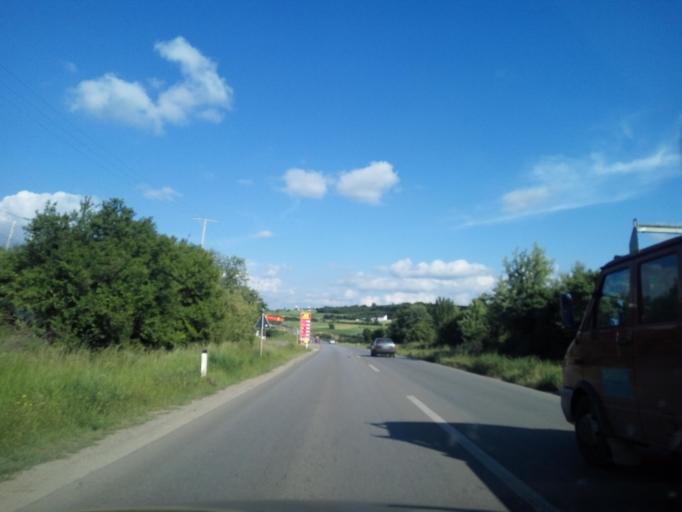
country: XK
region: Pec
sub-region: Komuna e Klines
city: Klina
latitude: 42.5901
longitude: 20.6662
